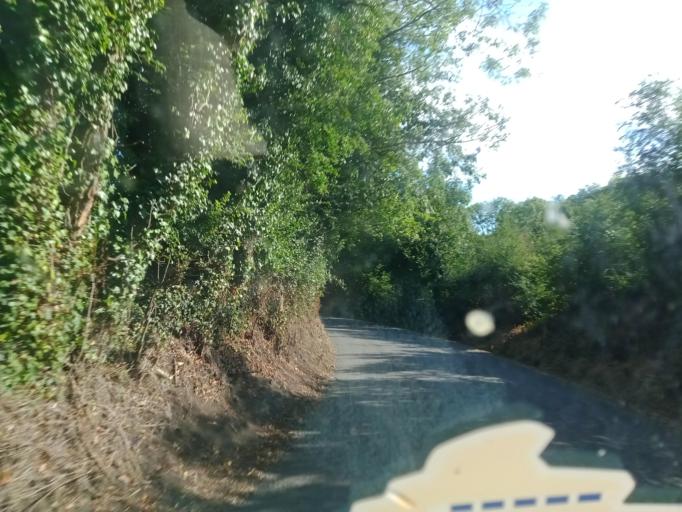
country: IE
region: Leinster
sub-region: Kilkenny
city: Ballyragget
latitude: 52.7835
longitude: -7.3920
